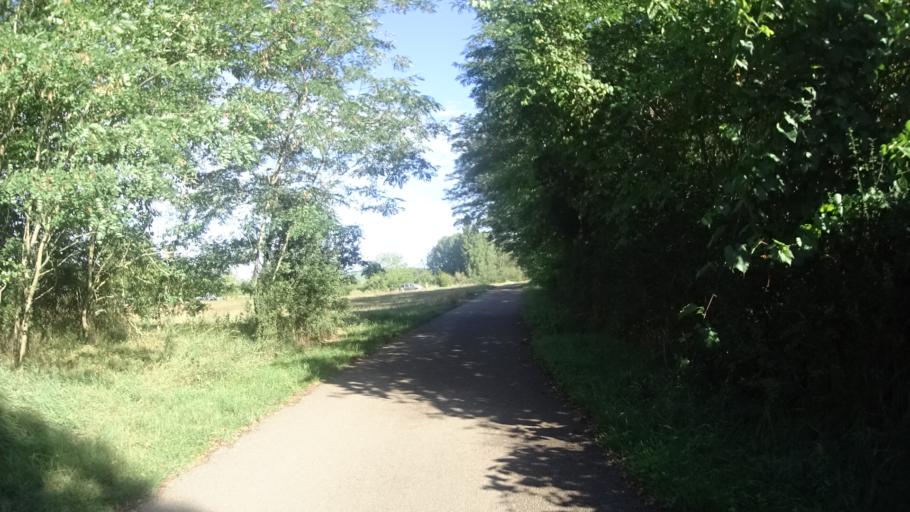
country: FR
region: Centre
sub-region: Departement du Cher
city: Sancerre
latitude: 47.3186
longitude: 2.8704
